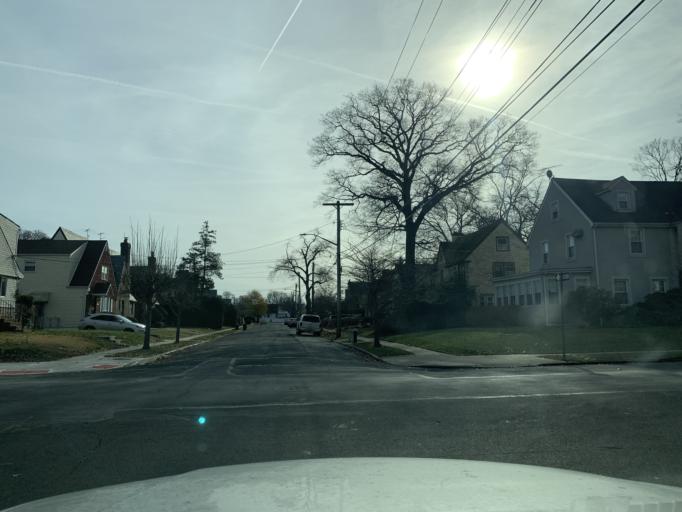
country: US
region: New York
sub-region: Queens County
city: Jamaica
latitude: 40.6945
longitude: -73.7735
